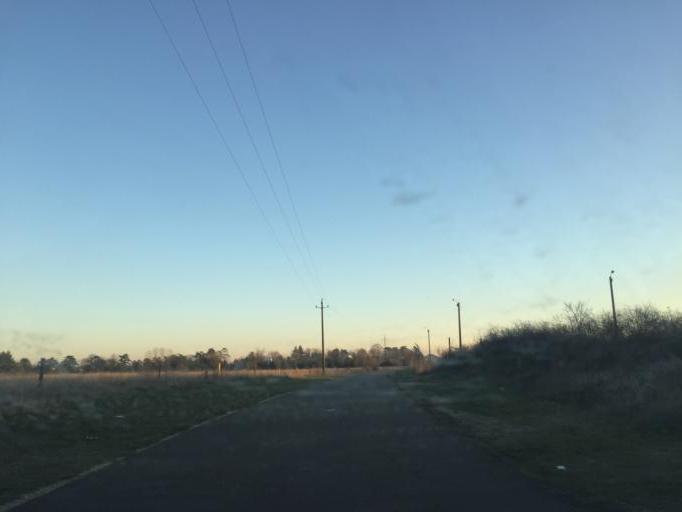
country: FR
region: Rhone-Alpes
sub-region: Departement de l'Ain
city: Beligneux
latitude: 45.8571
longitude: 5.1395
